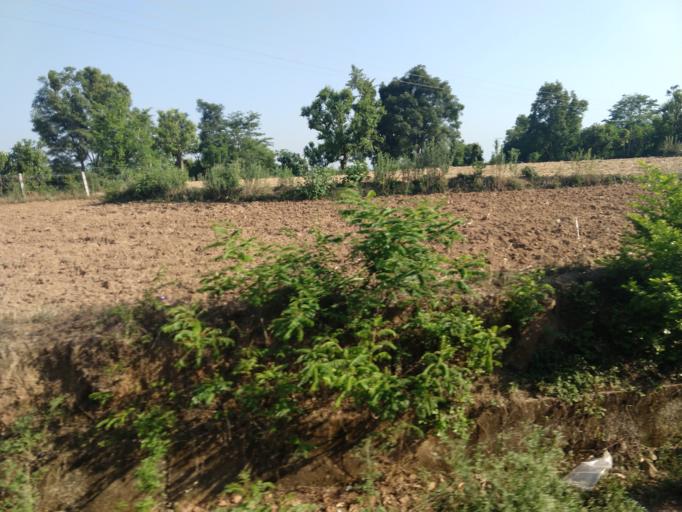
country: IN
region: Himachal Pradesh
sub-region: Chamba
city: Chowari
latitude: 32.3751
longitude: 75.9296
